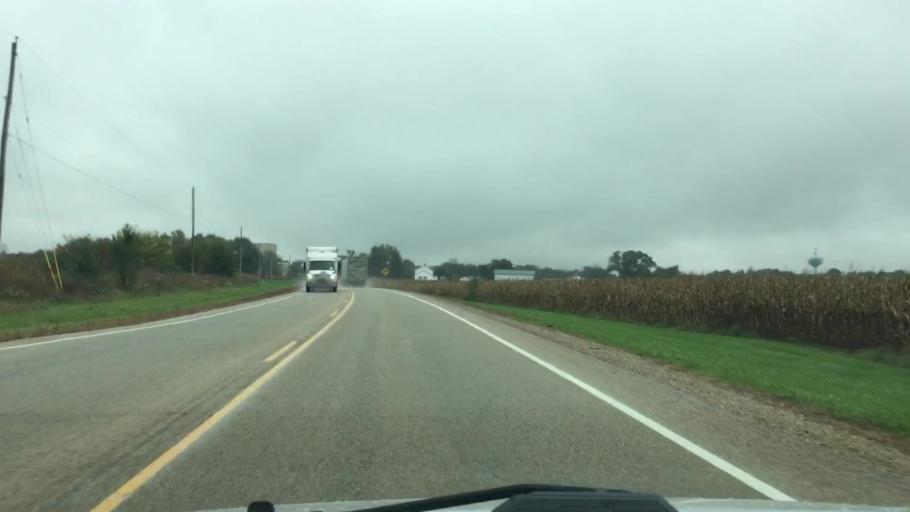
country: US
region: Wisconsin
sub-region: Walworth County
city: Whitewater
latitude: 42.8468
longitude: -88.7187
